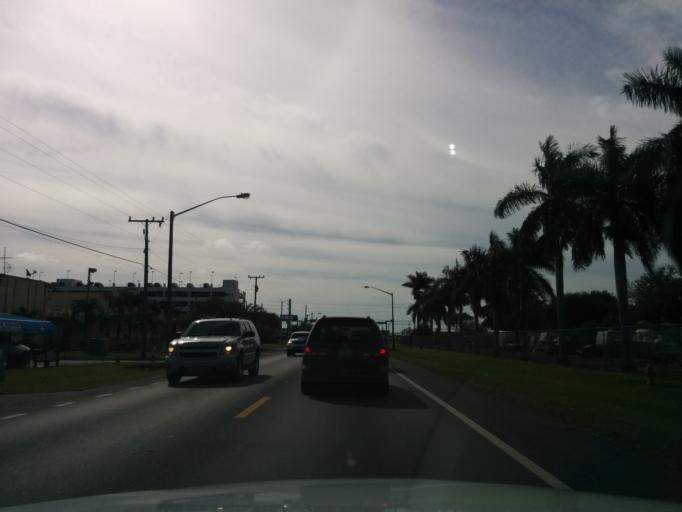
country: US
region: Florida
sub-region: Miami-Dade County
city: Florida City
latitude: 25.4567
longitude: -80.4773
